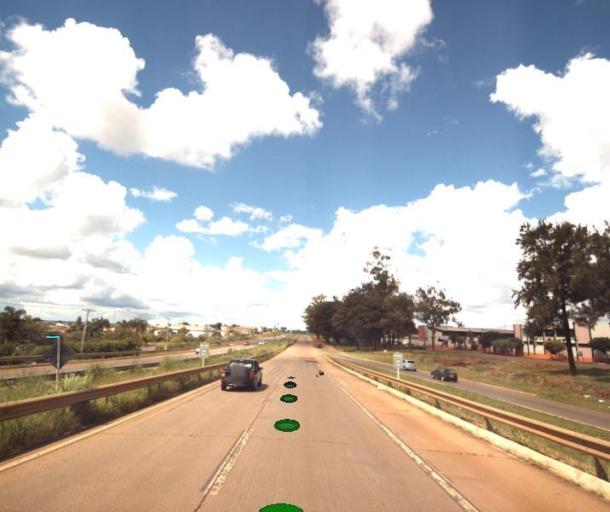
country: BR
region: Goias
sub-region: Anapolis
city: Anapolis
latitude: -16.3538
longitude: -48.9267
